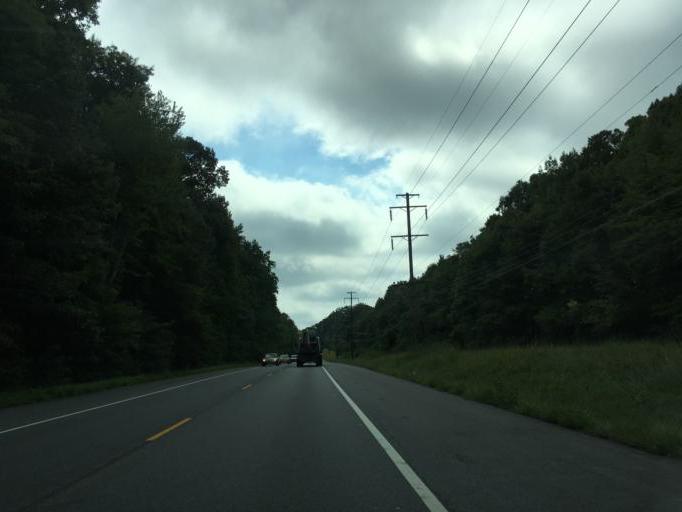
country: US
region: Maryland
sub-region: Anne Arundel County
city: Crownsville
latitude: 39.0186
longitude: -76.5836
